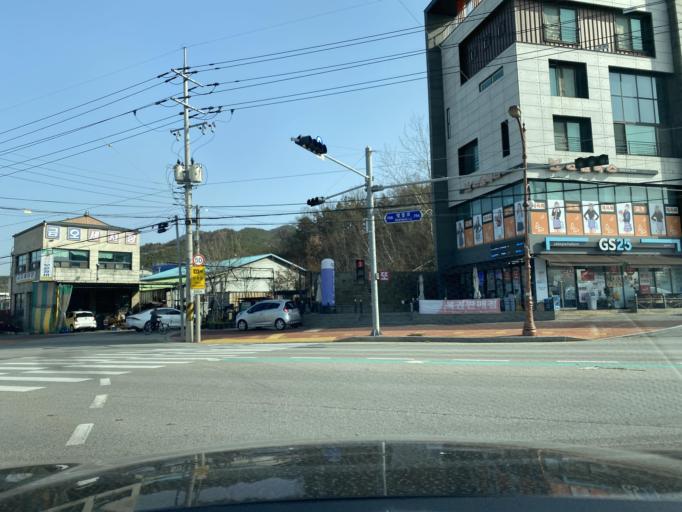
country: KR
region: Chungcheongnam-do
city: Yesan
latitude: 36.6978
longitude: 126.8373
